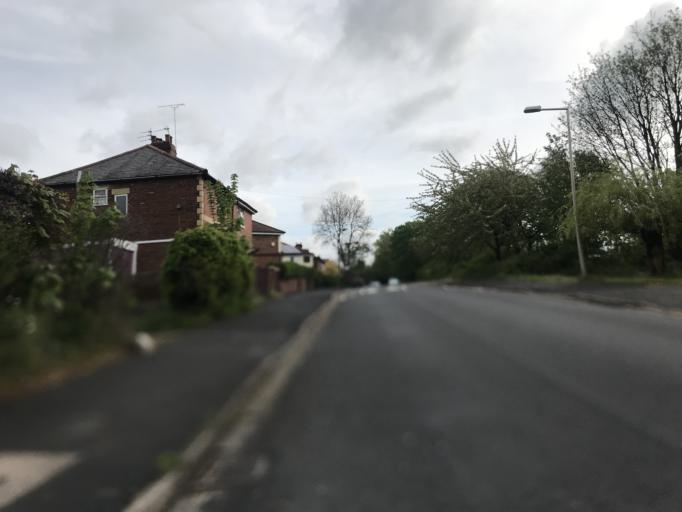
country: GB
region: England
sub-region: Borough of Stockport
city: Cheadle Heath
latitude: 53.4085
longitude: -2.1890
